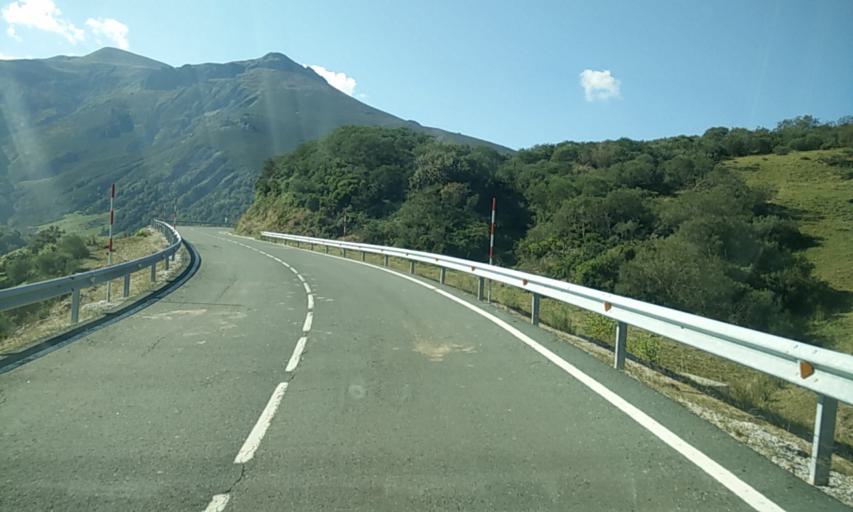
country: ES
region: Cantabria
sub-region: Provincia de Cantabria
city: Camaleno
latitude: 43.0743
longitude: -4.7397
